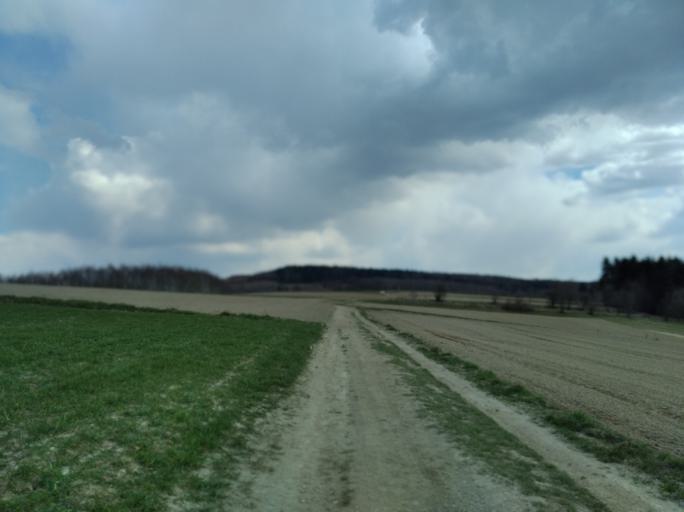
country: PL
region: Subcarpathian Voivodeship
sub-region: Powiat strzyzowski
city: Strzyzow
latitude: 49.9106
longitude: 21.7576
